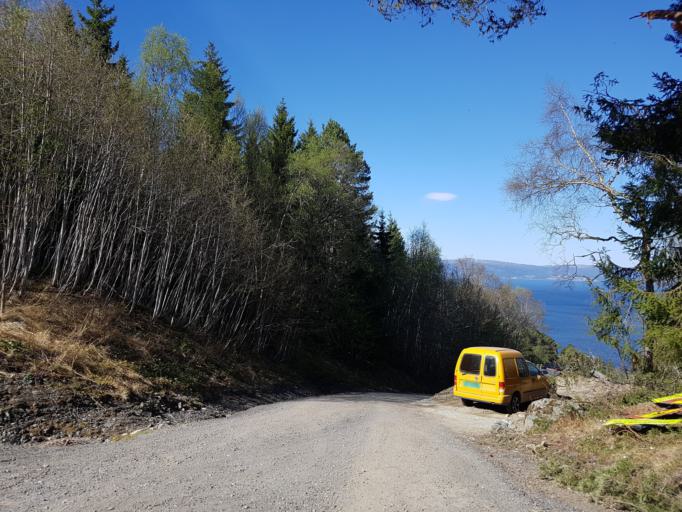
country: NO
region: Sor-Trondelag
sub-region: Trondheim
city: Trondheim
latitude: 63.4479
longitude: 10.3018
